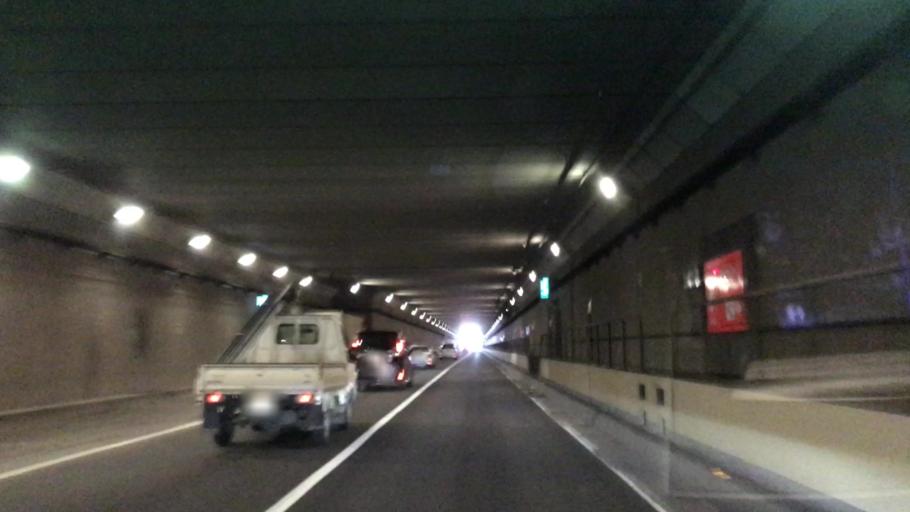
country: JP
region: Hokkaido
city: Sapporo
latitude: 43.0588
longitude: 141.3576
